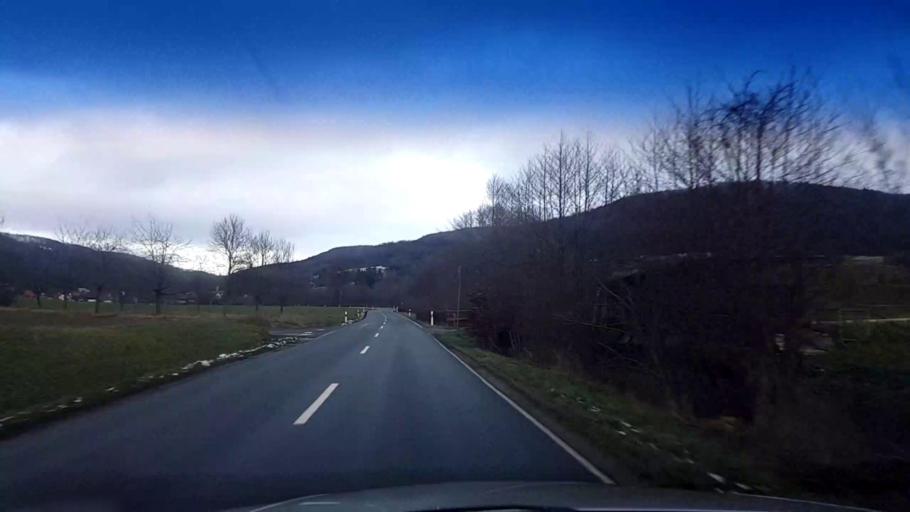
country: DE
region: Bavaria
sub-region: Upper Franconia
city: Buttenheim
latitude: 49.8243
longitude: 11.0789
